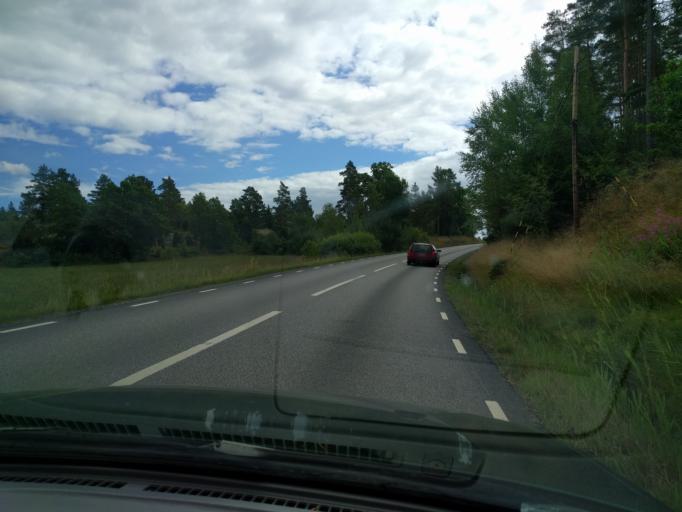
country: SE
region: Soedermanland
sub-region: Nykopings Kommun
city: Svalsta
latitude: 58.5192
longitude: 16.7929
